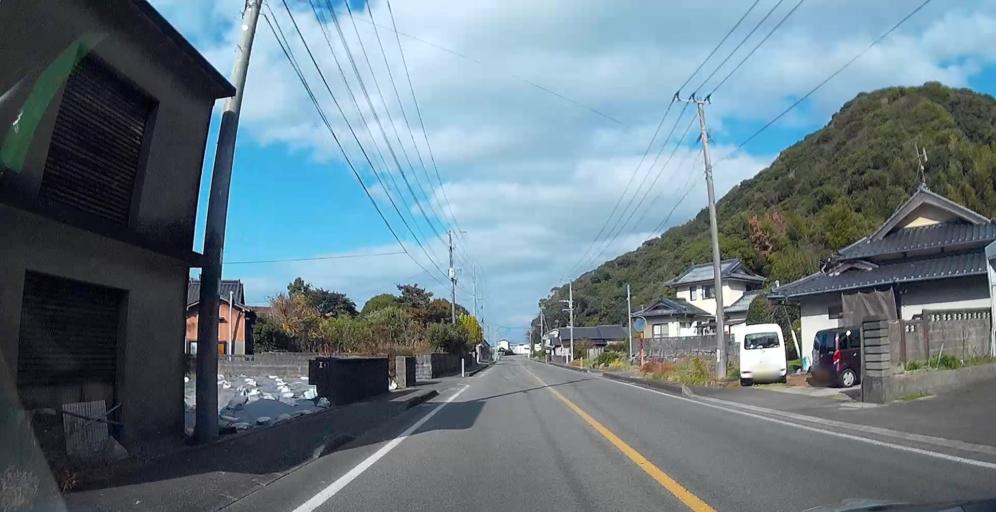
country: JP
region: Kumamoto
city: Yatsushiro
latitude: 32.4185
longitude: 130.5507
